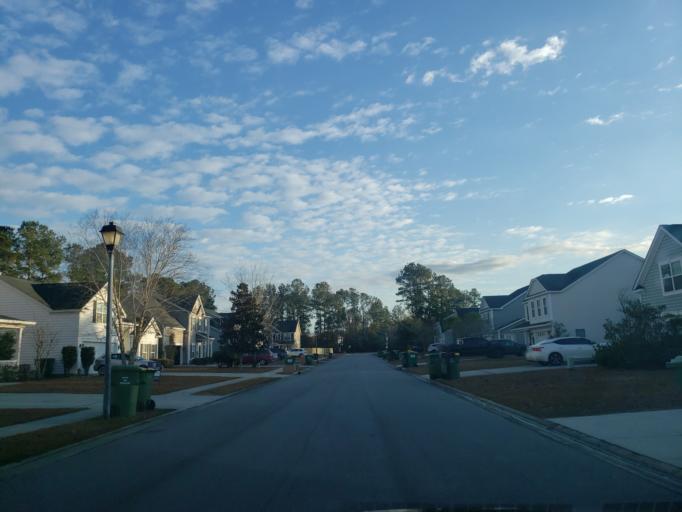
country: US
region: Georgia
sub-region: Chatham County
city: Bloomingdale
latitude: 32.1566
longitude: -81.2673
